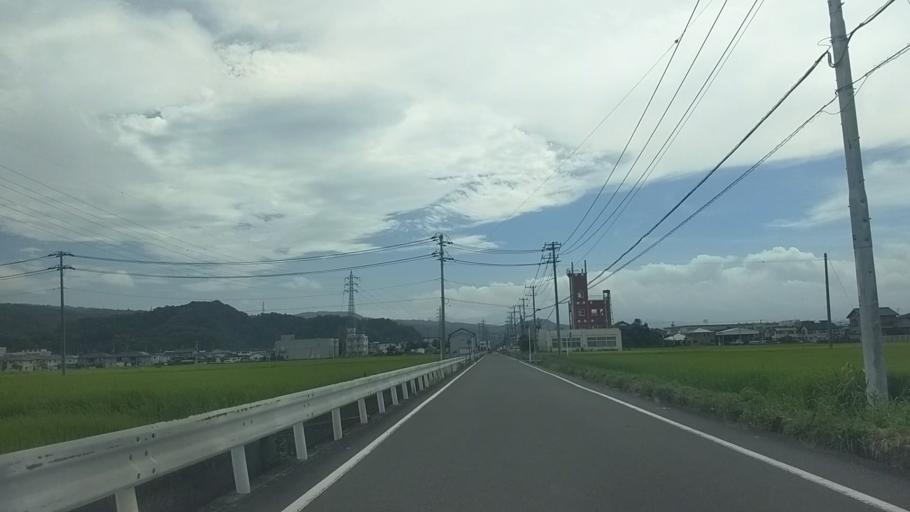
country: JP
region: Shizuoka
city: Mishima
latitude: 35.0608
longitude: 138.9478
